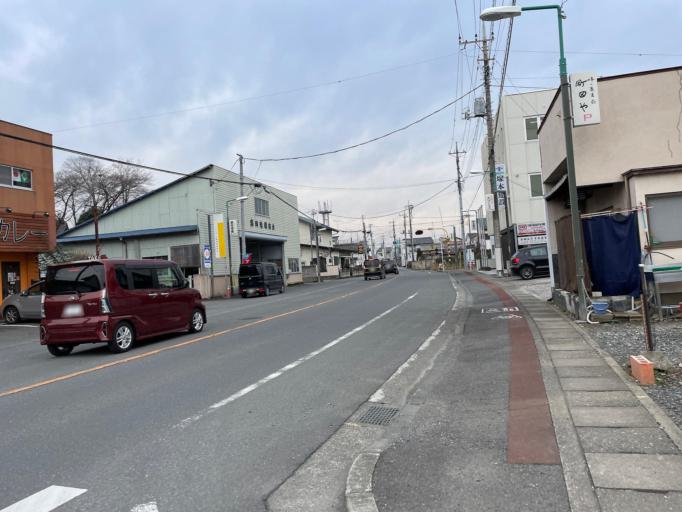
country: JP
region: Gunma
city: Fujioka
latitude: 36.2432
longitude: 139.0841
